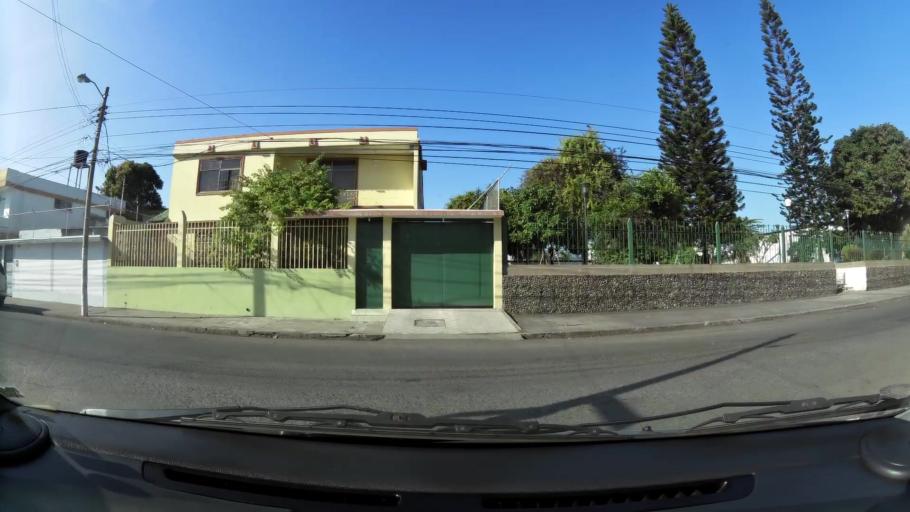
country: EC
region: Guayas
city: Eloy Alfaro
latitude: -2.1702
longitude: -79.8869
